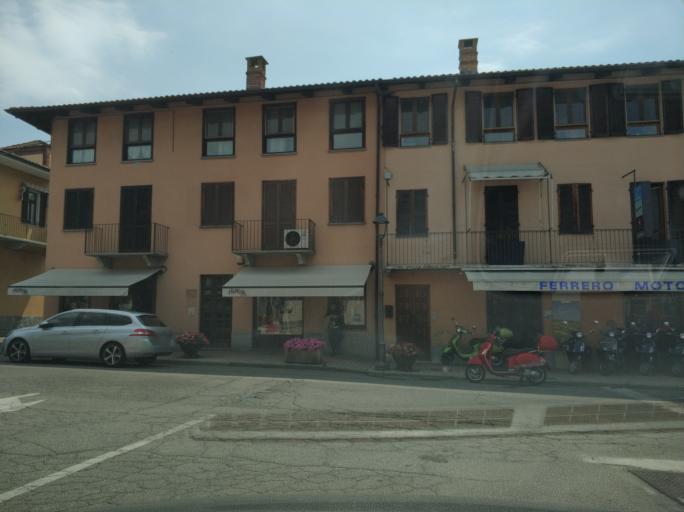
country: IT
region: Piedmont
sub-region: Provincia di Cuneo
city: Canale
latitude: 44.7966
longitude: 7.9896
